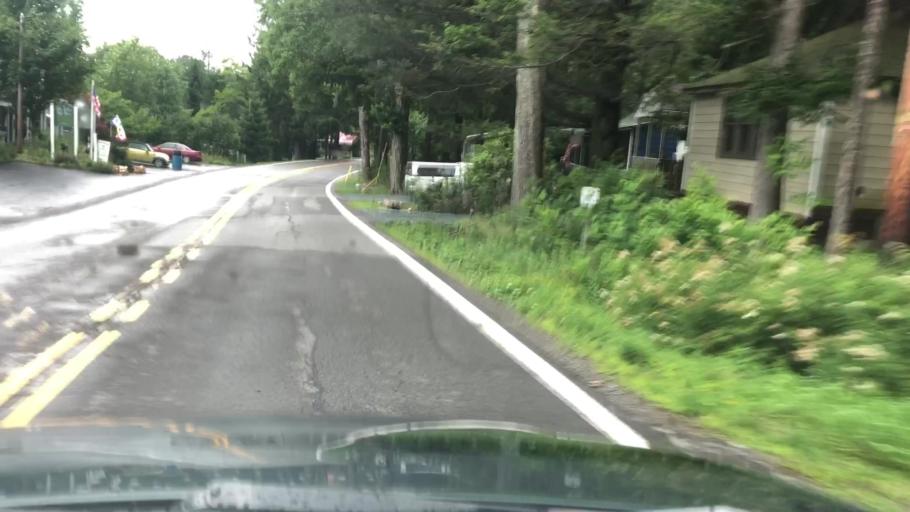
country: US
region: Pennsylvania
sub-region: Monroe County
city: Mountainhome
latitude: 41.3094
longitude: -75.2108
